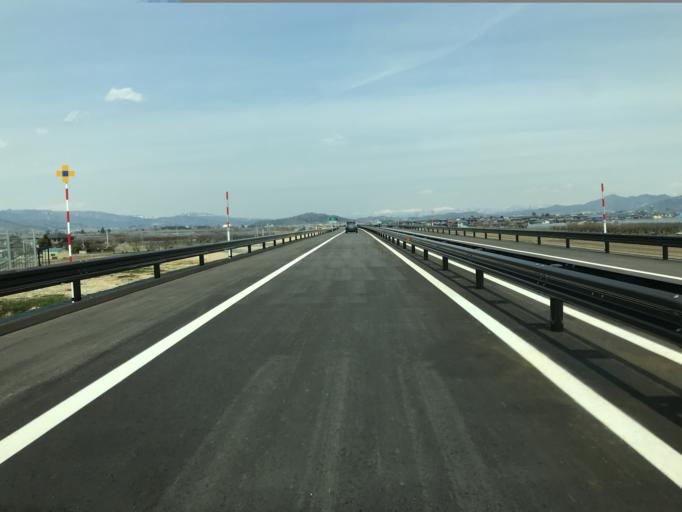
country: JP
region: Yamagata
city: Higashine
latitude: 38.4358
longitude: 140.3535
